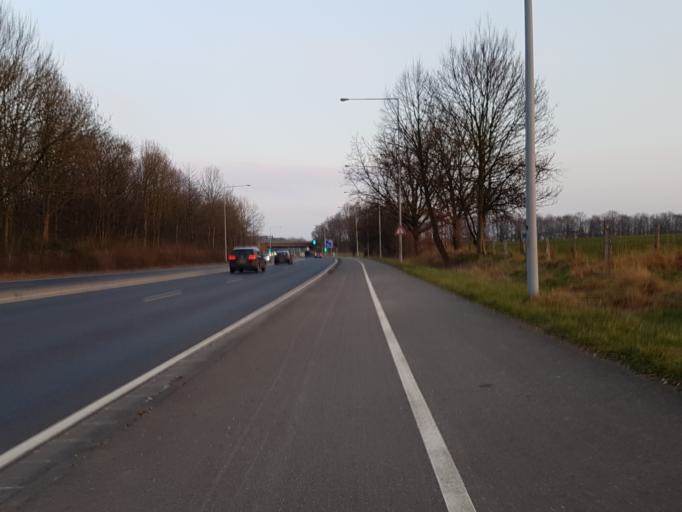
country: DE
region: North Rhine-Westphalia
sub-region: Regierungsbezirk Koln
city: Wurselen
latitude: 50.7873
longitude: 6.1225
